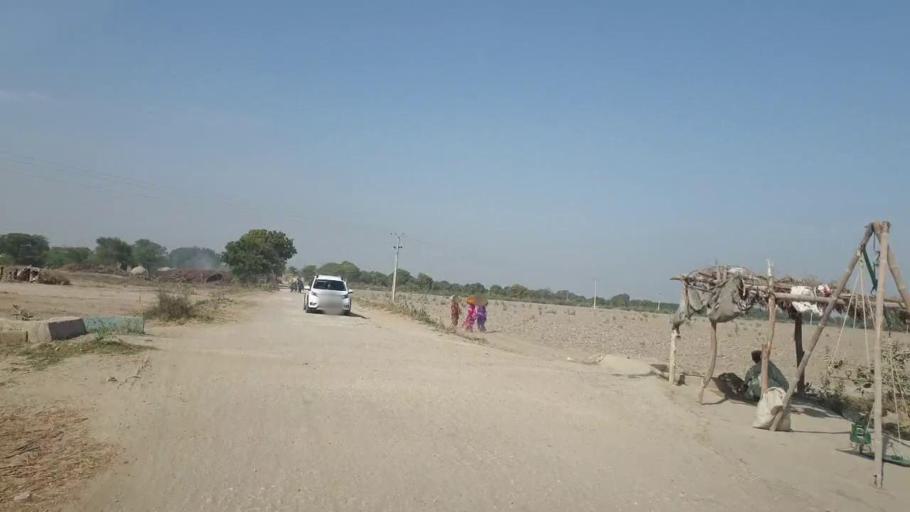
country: PK
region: Sindh
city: Nabisar
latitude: 25.0322
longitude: 69.5245
